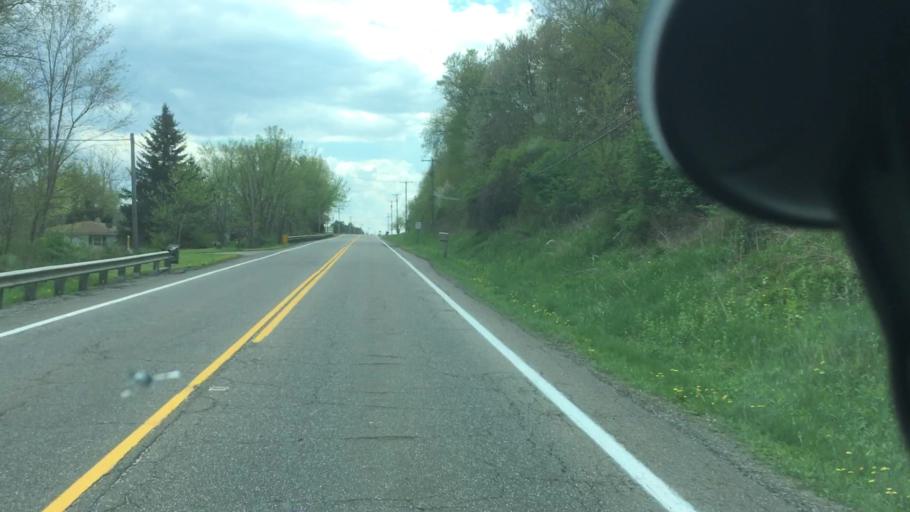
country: US
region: Ohio
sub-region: Columbiana County
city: Columbiana
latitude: 40.9113
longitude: -80.6938
